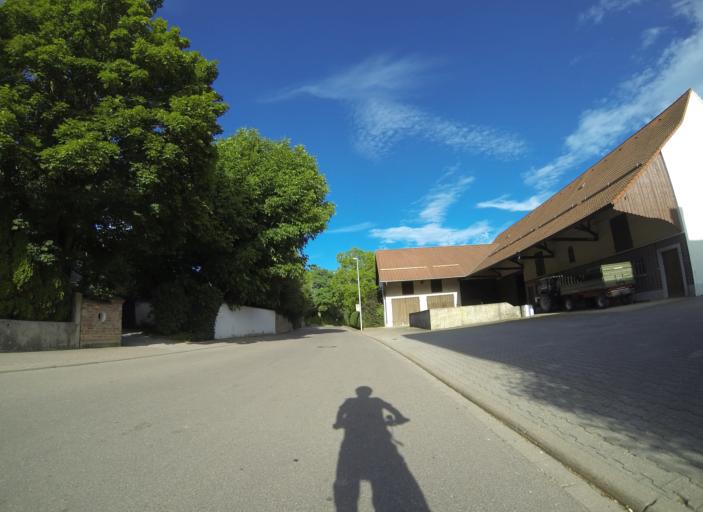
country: DE
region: Baden-Wuerttemberg
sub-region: Tuebingen Region
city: Altheim
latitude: 48.3275
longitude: 9.7711
